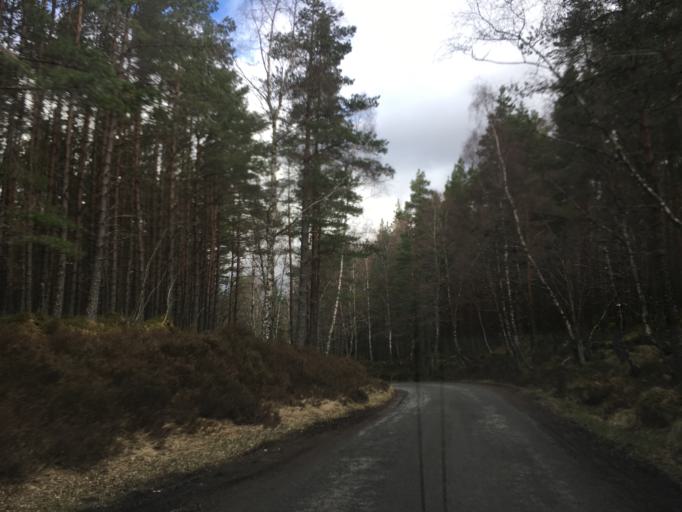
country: GB
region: Scotland
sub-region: Highland
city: Aviemore
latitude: 57.1046
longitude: -3.9222
